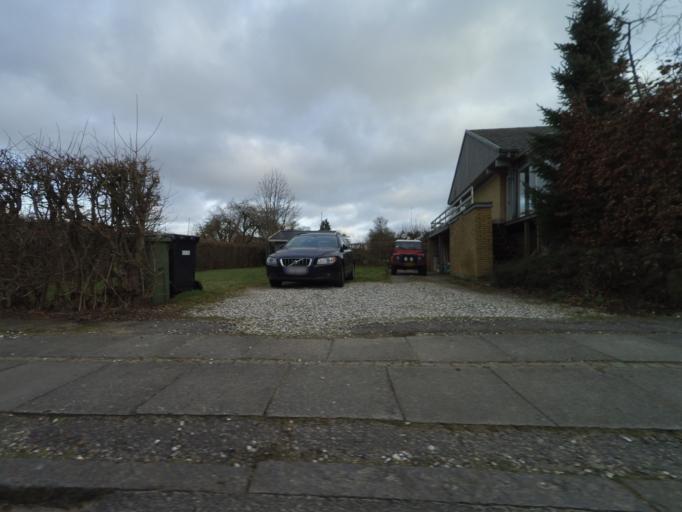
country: DK
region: Central Jutland
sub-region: Arhus Kommune
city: Arhus
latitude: 56.1223
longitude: 10.1771
